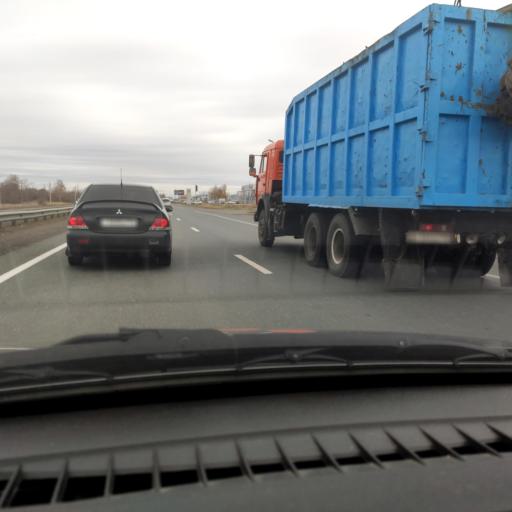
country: RU
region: Samara
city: Tol'yatti
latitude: 53.5732
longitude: 49.3896
